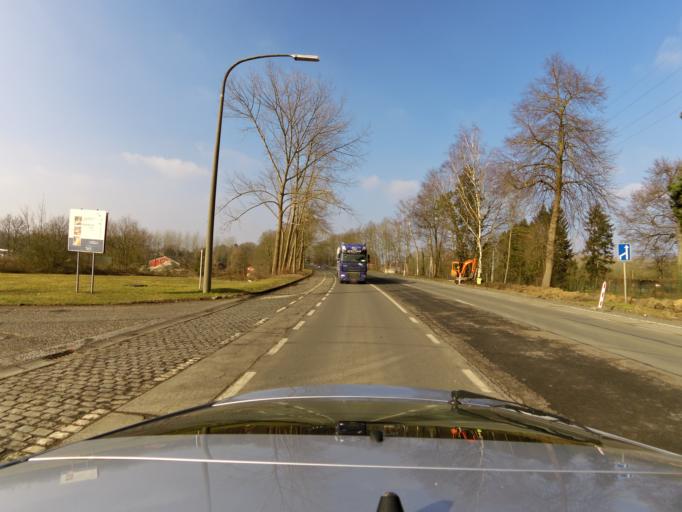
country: BE
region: Wallonia
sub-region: Province du Hainaut
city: Saint-Ghislain
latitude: 50.4786
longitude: 3.8358
